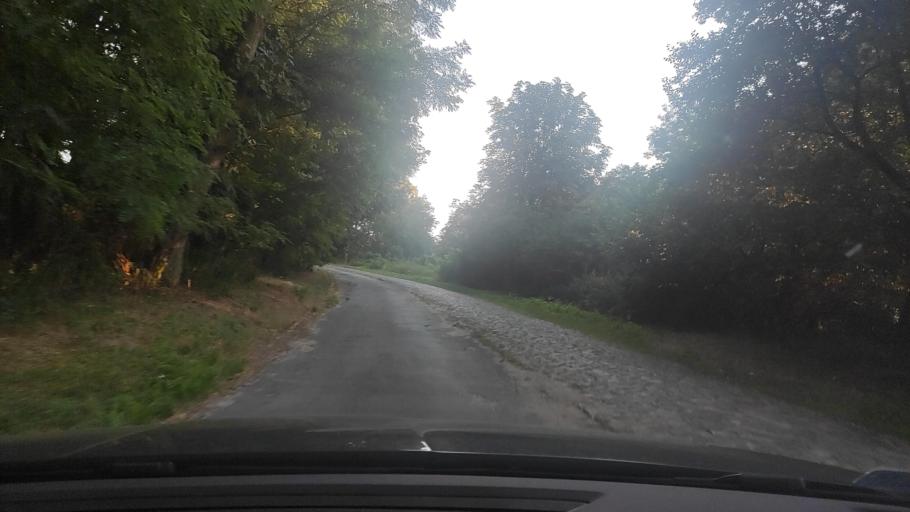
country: PL
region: Greater Poland Voivodeship
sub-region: Powiat poznanski
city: Kobylnica
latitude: 52.4449
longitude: 17.1280
